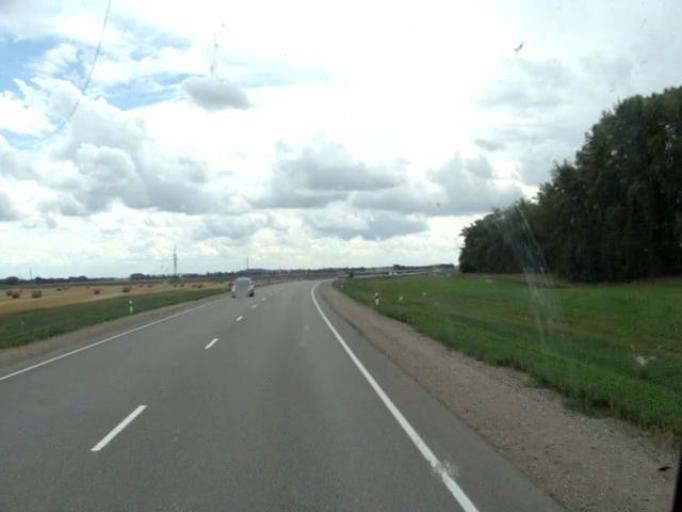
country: RU
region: Altai Krai
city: Shubenka
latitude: 52.6807
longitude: 85.0480
